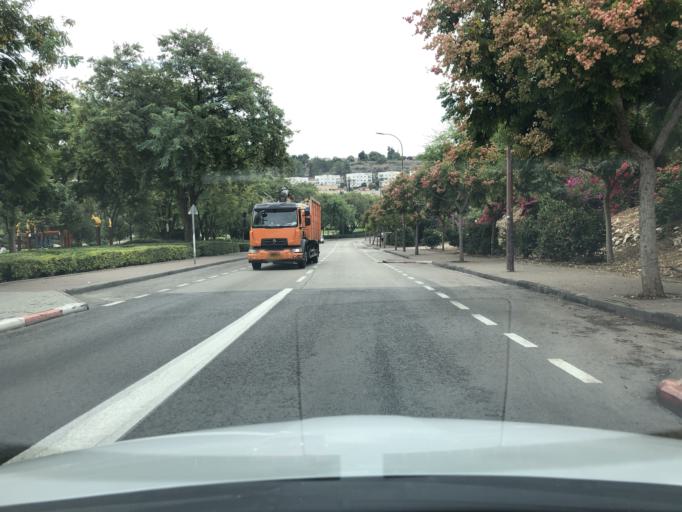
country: IL
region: Central District
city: Modiin
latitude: 31.8991
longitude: 35.0159
